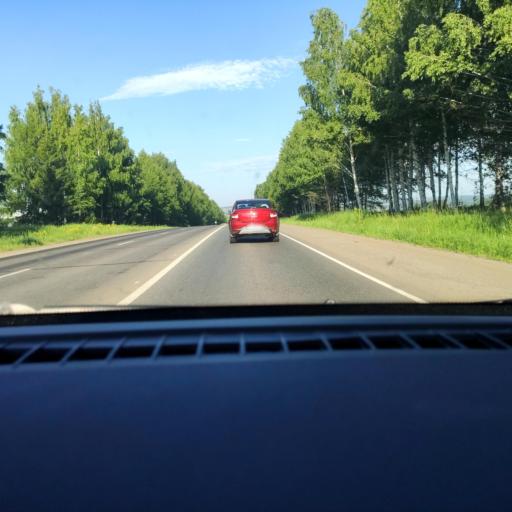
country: RU
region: Udmurtiya
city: Khokhryaki
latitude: 56.9152
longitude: 53.4164
